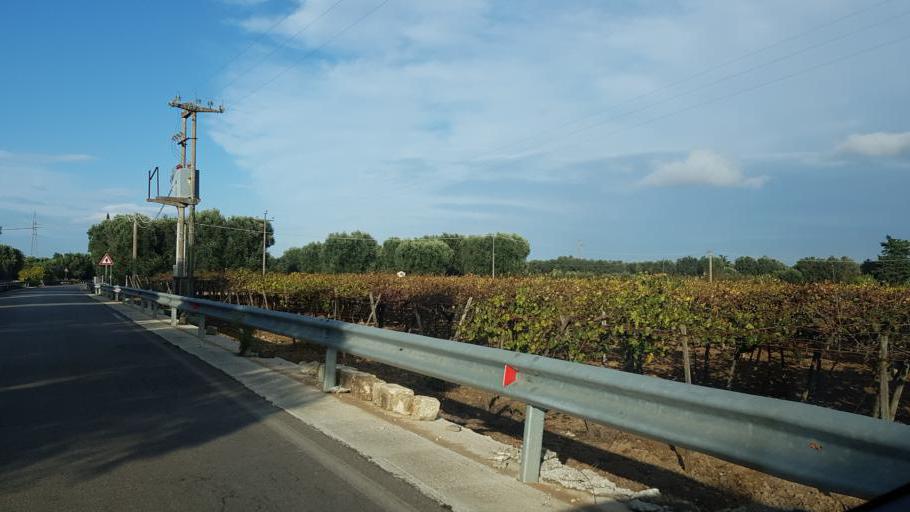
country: IT
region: Apulia
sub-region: Provincia di Brindisi
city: Oria
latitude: 40.5226
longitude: 17.6530
